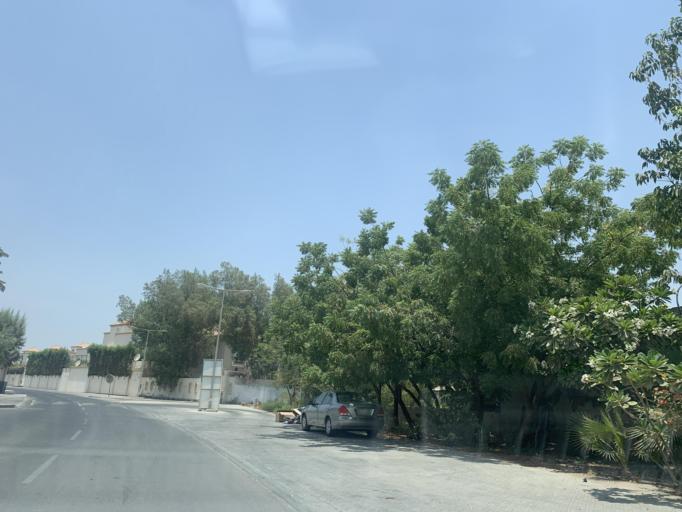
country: BH
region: Manama
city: Jidd Hafs
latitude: 26.2126
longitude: 50.4737
